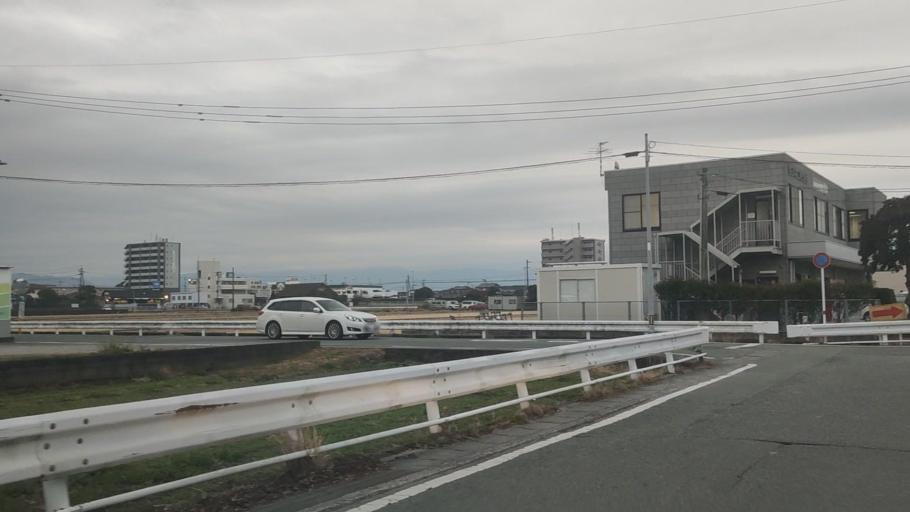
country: JP
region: Kumamoto
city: Kumamoto
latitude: 32.7670
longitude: 130.7100
